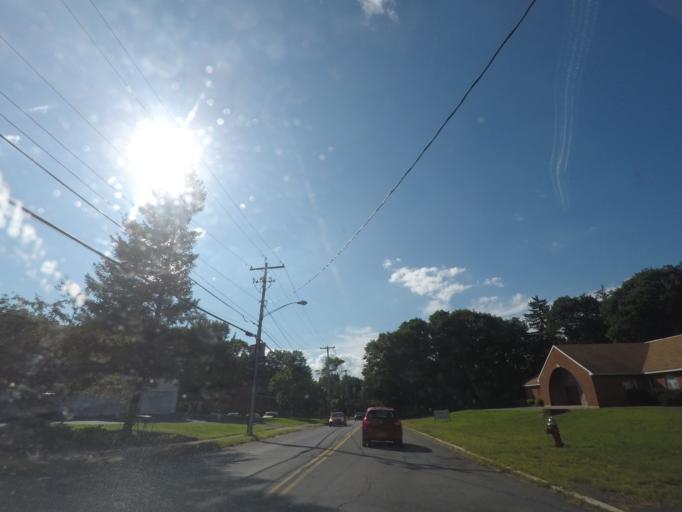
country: US
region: New York
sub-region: Rensselaer County
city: Wynantskill
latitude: 42.7099
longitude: -73.6656
